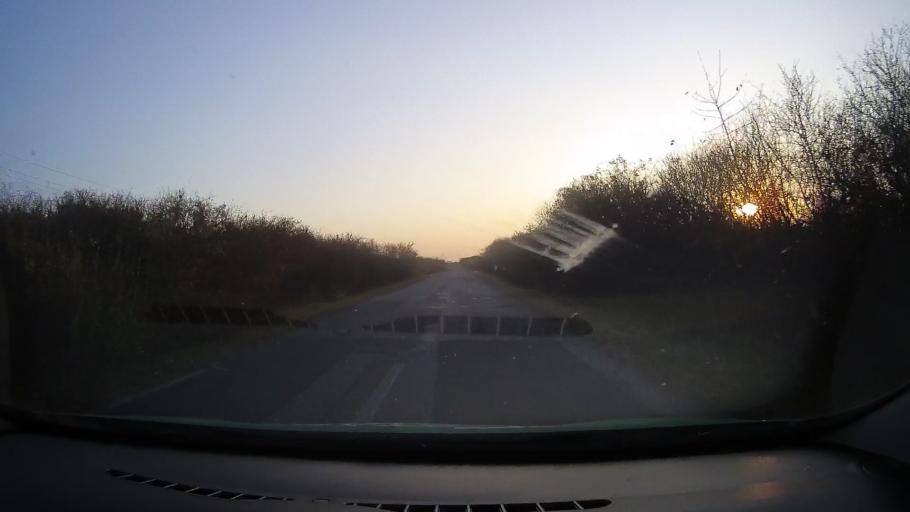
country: RO
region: Arad
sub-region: Comuna Seleus
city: Seleus
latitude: 46.4039
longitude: 21.7276
